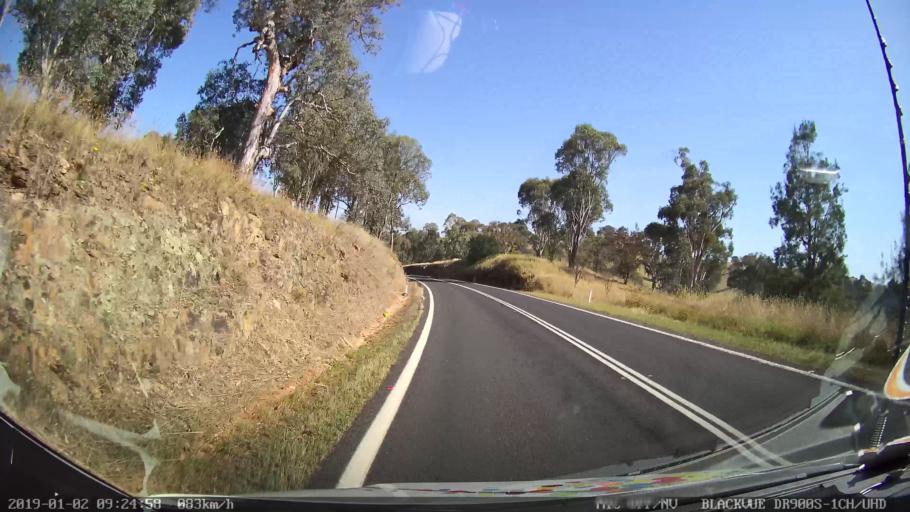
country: AU
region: New South Wales
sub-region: Tumut Shire
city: Tumut
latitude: -35.3701
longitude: 148.2919
